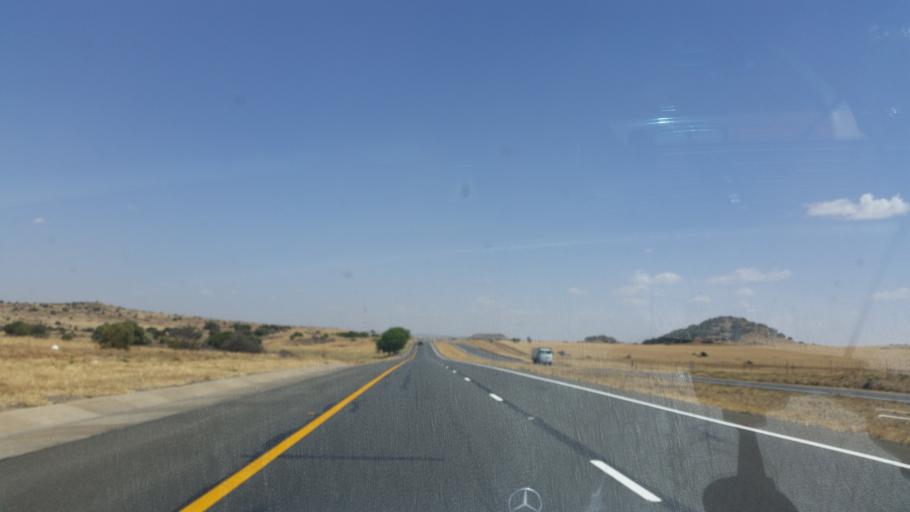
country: ZA
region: Orange Free State
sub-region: Lejweleputswa District Municipality
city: Brandfort
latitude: -28.9260
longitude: 26.4331
